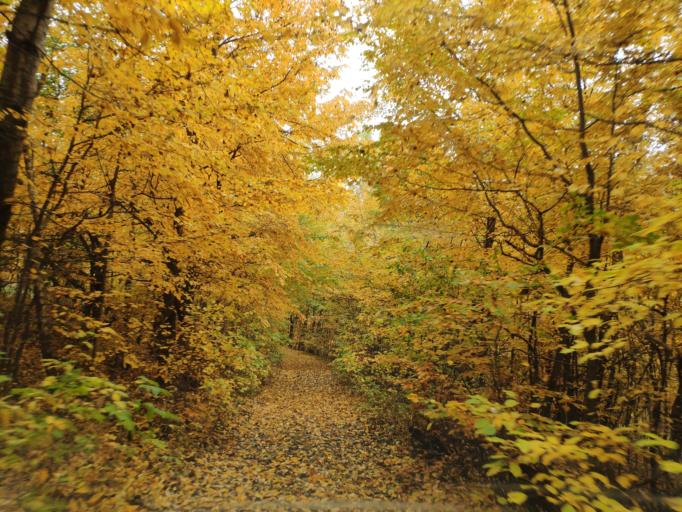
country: SK
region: Kosicky
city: Kosice
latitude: 48.7246
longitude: 21.1099
